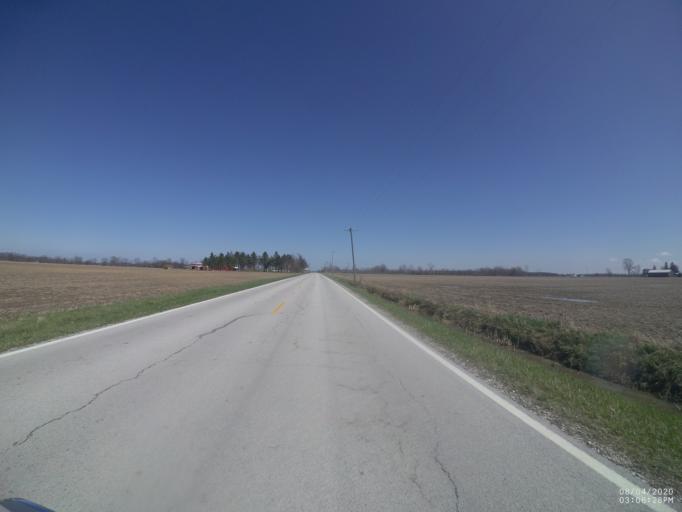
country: US
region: Ohio
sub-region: Sandusky County
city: Stony Prairie
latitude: 41.3038
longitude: -83.2383
